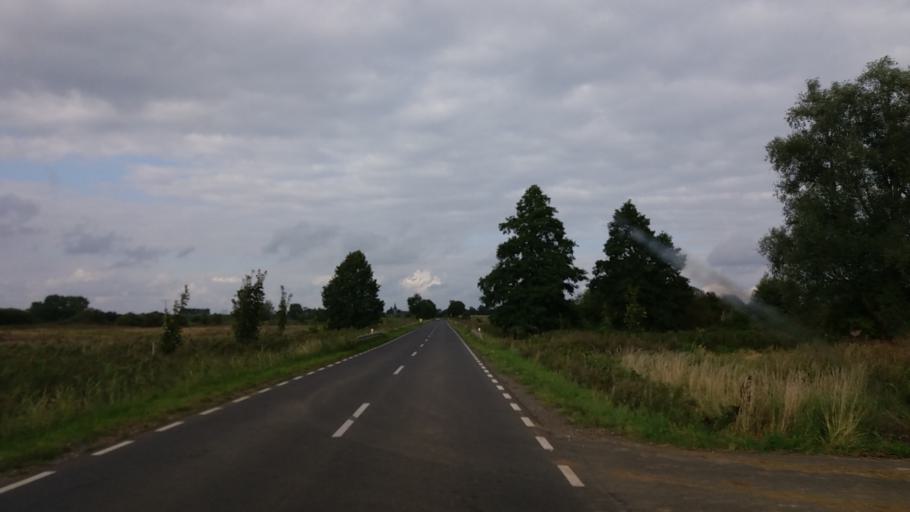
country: PL
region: West Pomeranian Voivodeship
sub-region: Powiat choszczenski
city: Choszczno
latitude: 53.1198
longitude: 15.3583
